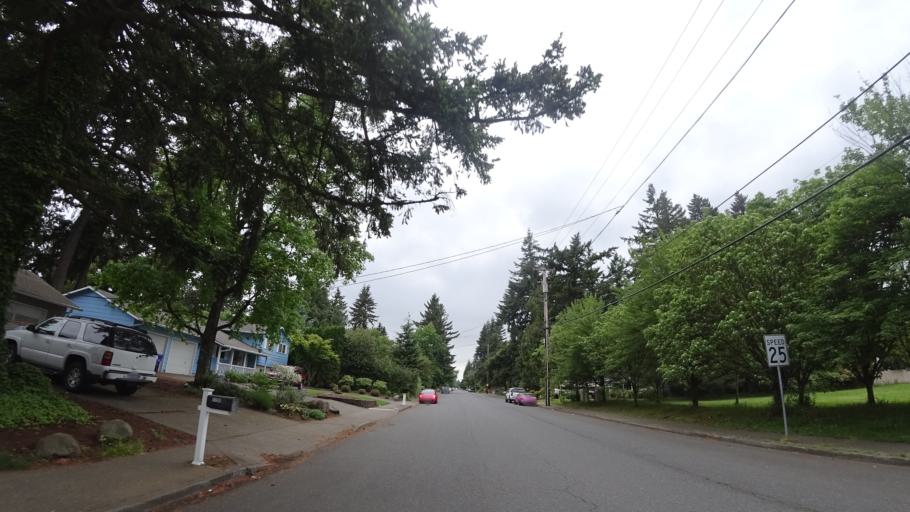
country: US
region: Oregon
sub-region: Multnomah County
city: Lents
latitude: 45.5112
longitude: -122.5211
